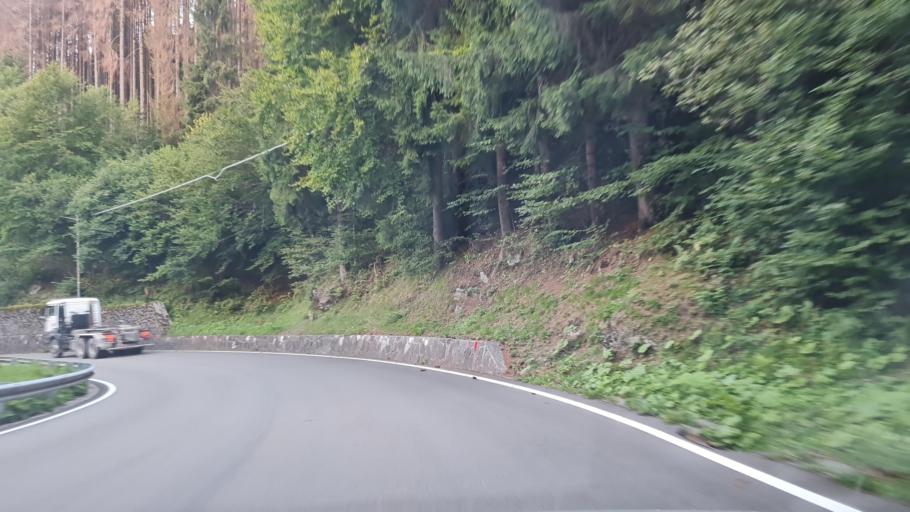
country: IT
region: Trentino-Alto Adige
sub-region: Provincia di Trento
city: Siror
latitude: 46.2195
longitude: 11.8121
